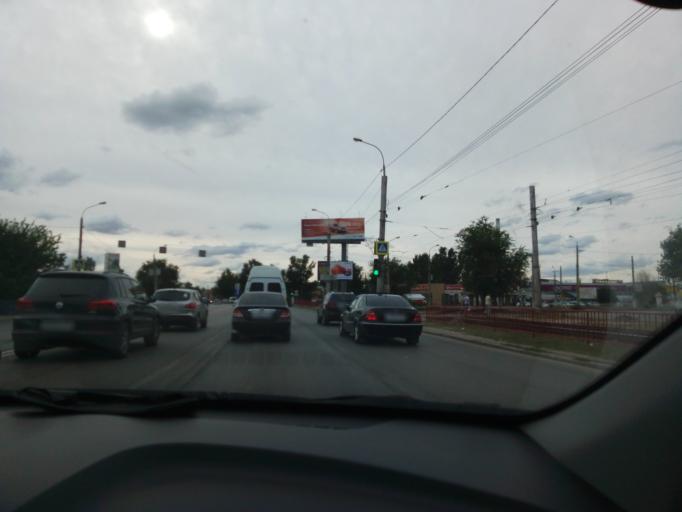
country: RU
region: Volgograd
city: Krasnoslobodsk
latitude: 48.5153
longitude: 44.5361
